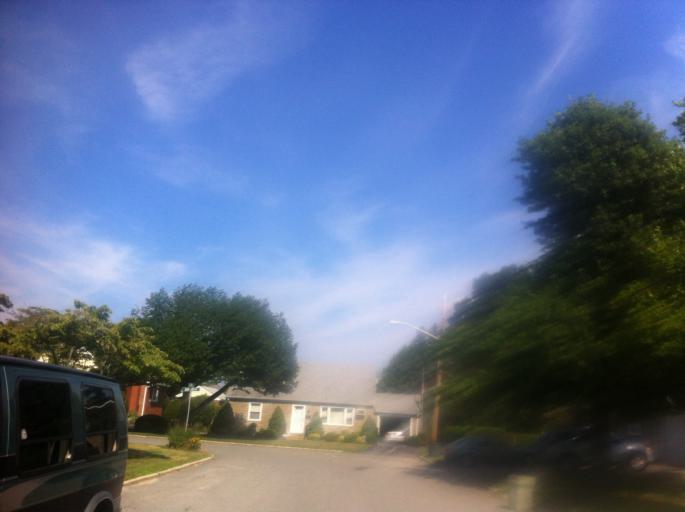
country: US
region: New York
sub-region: Nassau County
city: Locust Valley
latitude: 40.8563
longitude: -73.6104
